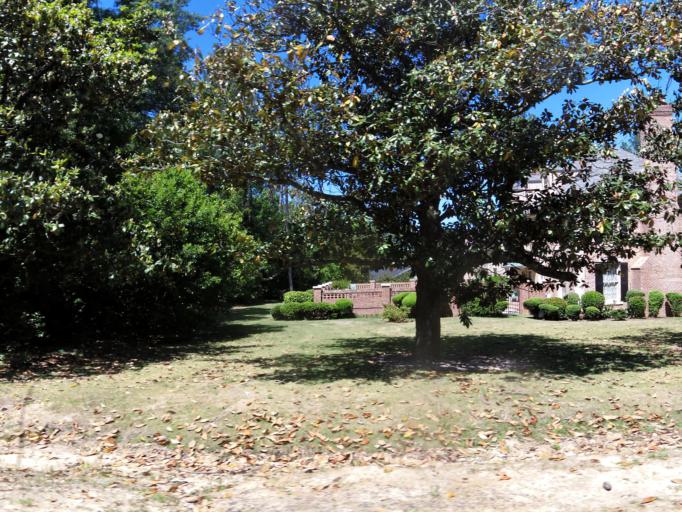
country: US
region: Georgia
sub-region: Columbia County
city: Martinez
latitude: 33.4894
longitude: -82.0292
